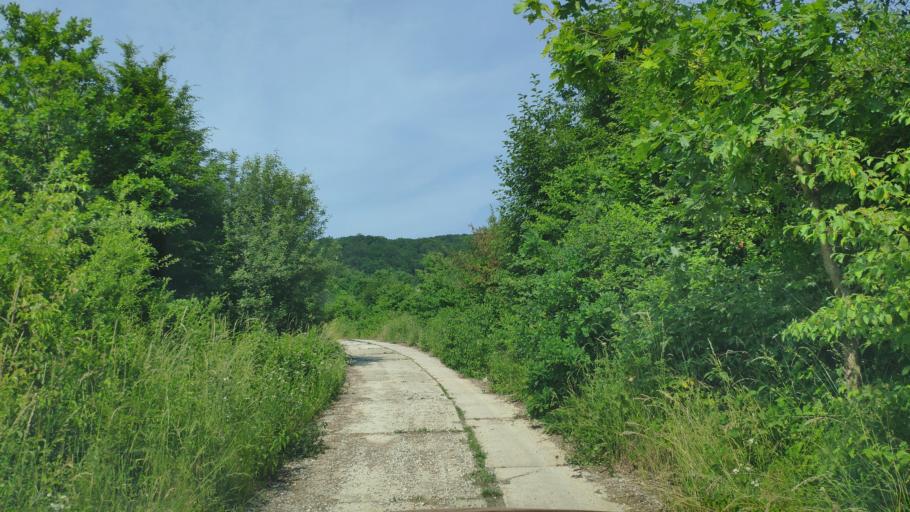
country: SK
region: Presovsky
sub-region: Okres Presov
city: Presov
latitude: 48.9642
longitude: 21.1430
